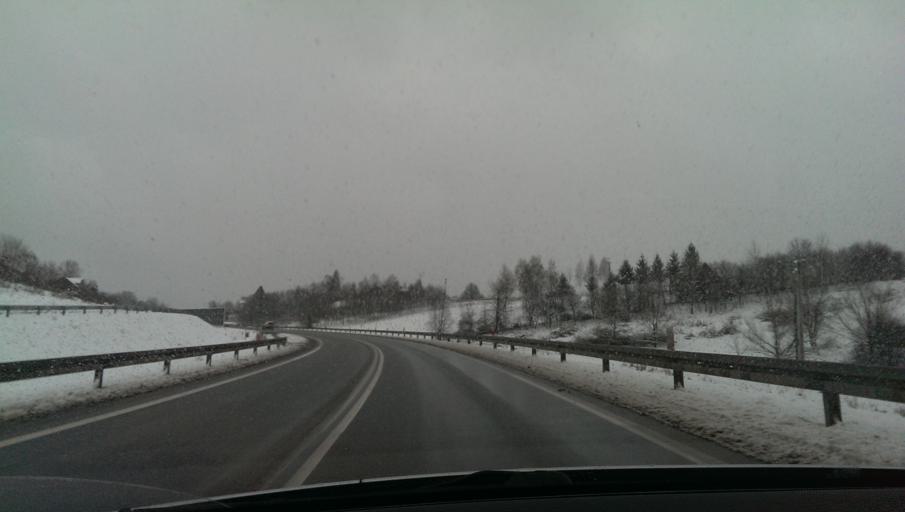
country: PL
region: Subcarpathian Voivodeship
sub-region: Powiat brzozowski
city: Brzozow
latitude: 49.6905
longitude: 22.0310
